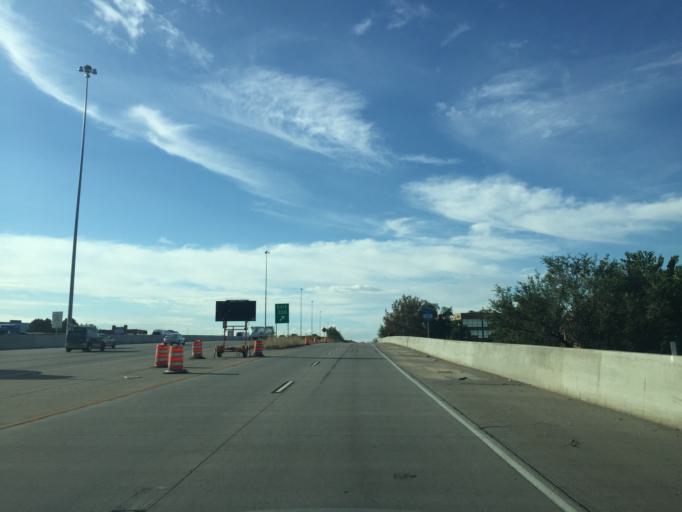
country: US
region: Utah
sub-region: Salt Lake County
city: Murray
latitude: 40.6592
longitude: -111.9017
